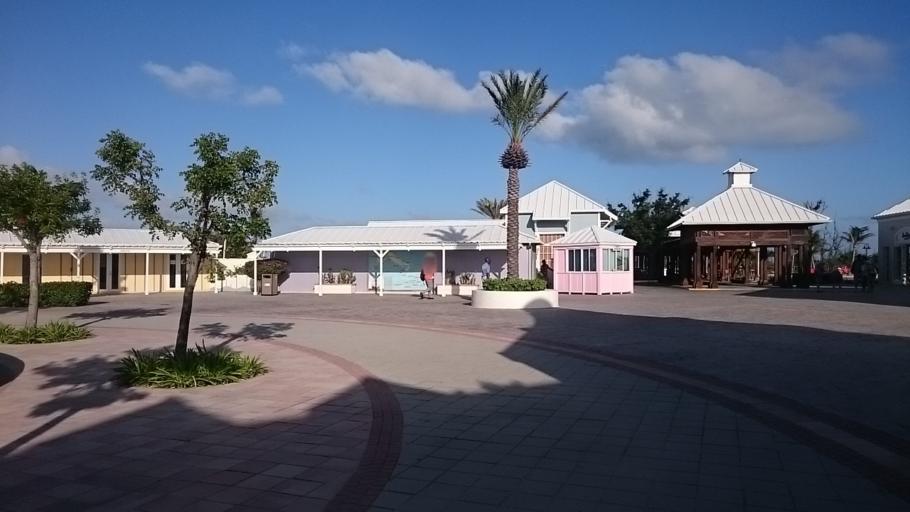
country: TC
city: Cockburn Town
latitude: 21.4279
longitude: -71.1446
